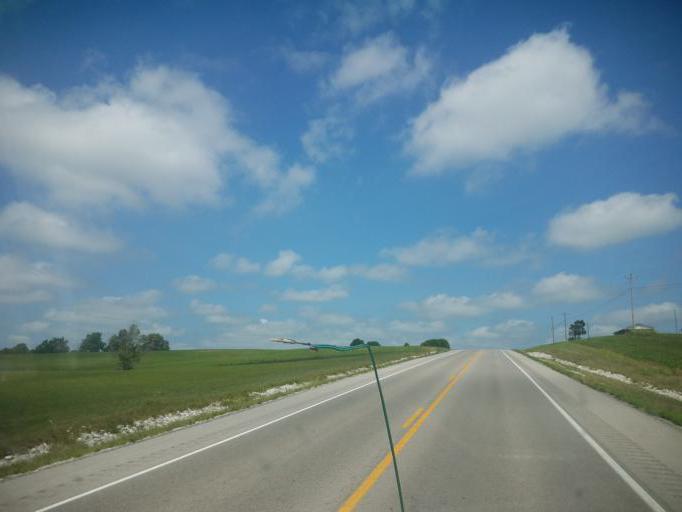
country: US
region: Kentucky
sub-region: Barren County
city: Glasgow
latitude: 36.9280
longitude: -85.8092
